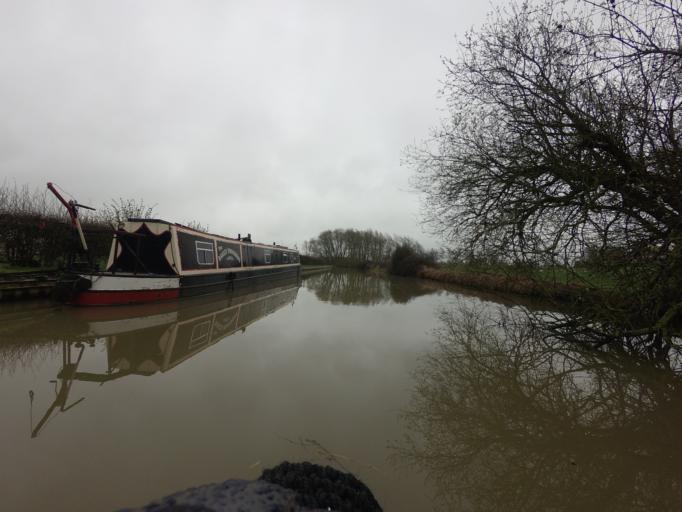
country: GB
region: England
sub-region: Milton Keynes
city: Castlethorpe
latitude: 52.0975
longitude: -0.8731
